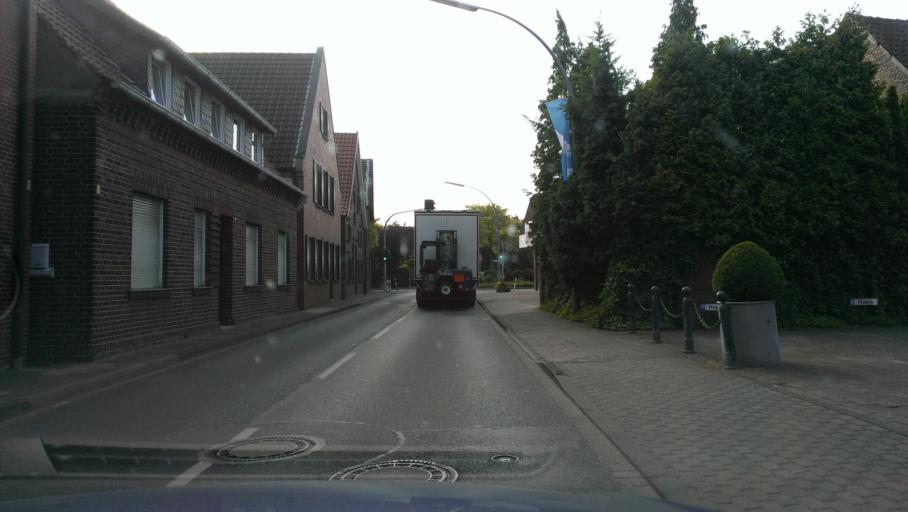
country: DE
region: North Rhine-Westphalia
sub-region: Regierungsbezirk Munster
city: Drensteinfurt
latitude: 51.8668
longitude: 7.7341
